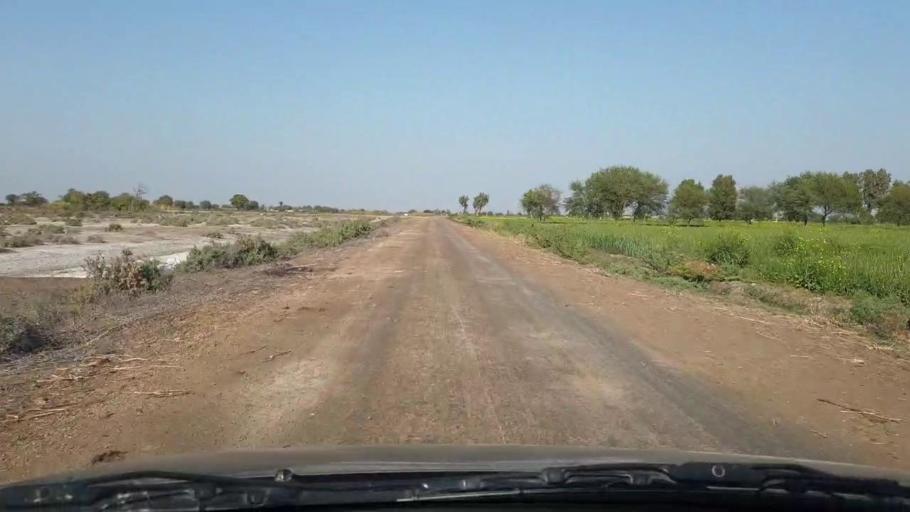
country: PK
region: Sindh
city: Samaro
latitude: 25.1643
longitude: 69.2824
